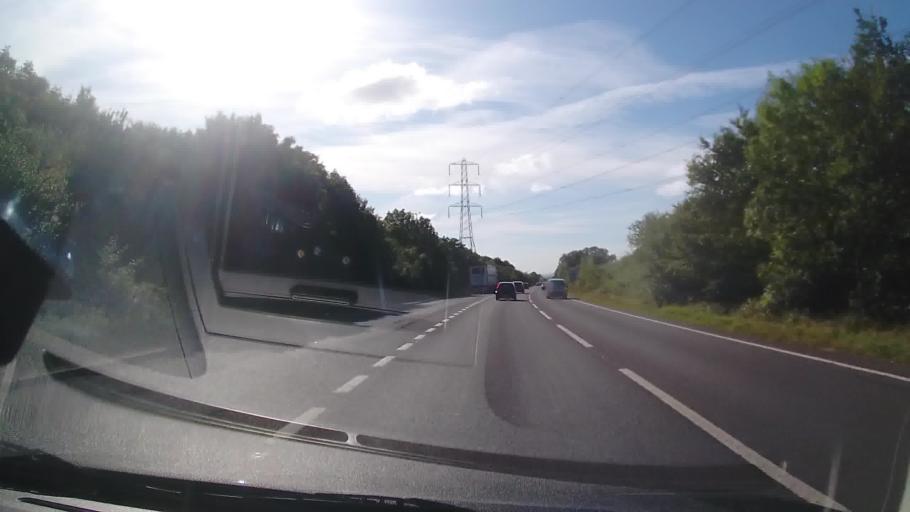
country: GB
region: England
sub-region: Shropshire
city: Astley
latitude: 52.7417
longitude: -2.7112
